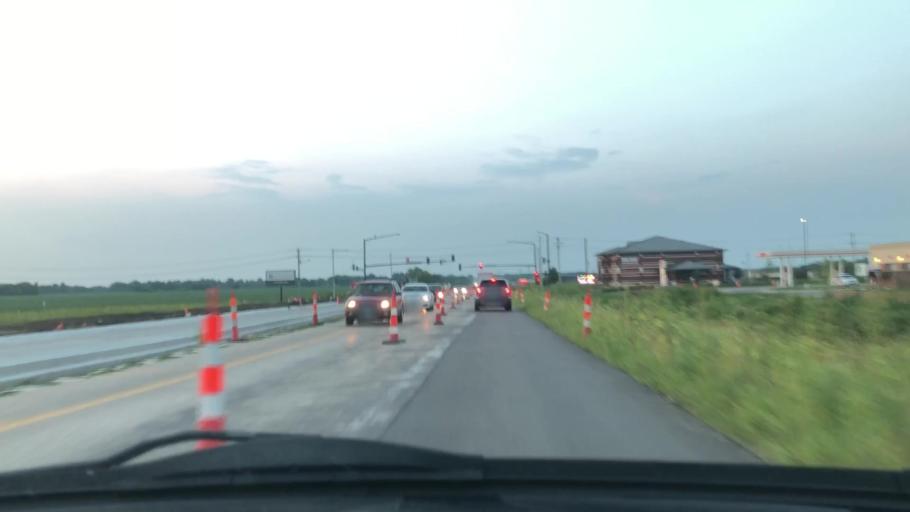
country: US
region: Iowa
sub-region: Johnson County
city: North Liberty
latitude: 41.7214
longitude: -91.6078
